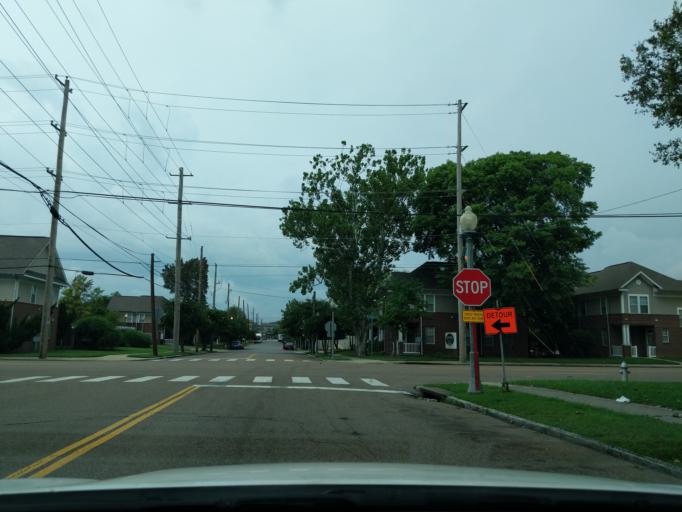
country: US
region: Tennessee
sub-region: Shelby County
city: Memphis
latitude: 35.1584
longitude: -90.0444
